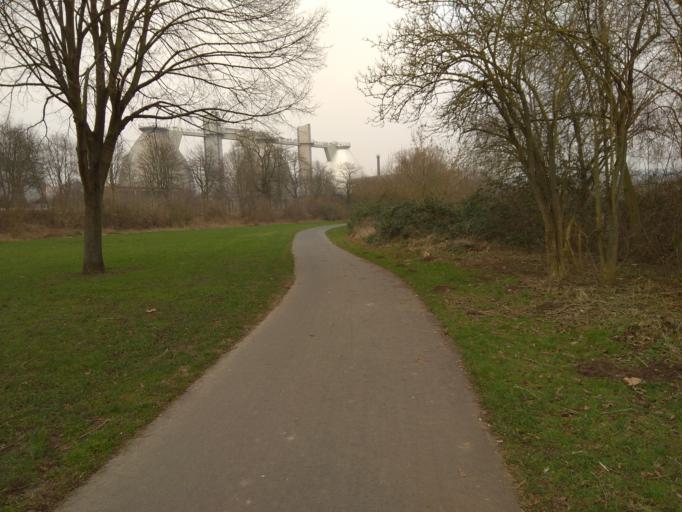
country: DE
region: Hesse
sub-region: Regierungsbezirk Kassel
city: Kassel
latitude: 51.3223
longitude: 9.5231
